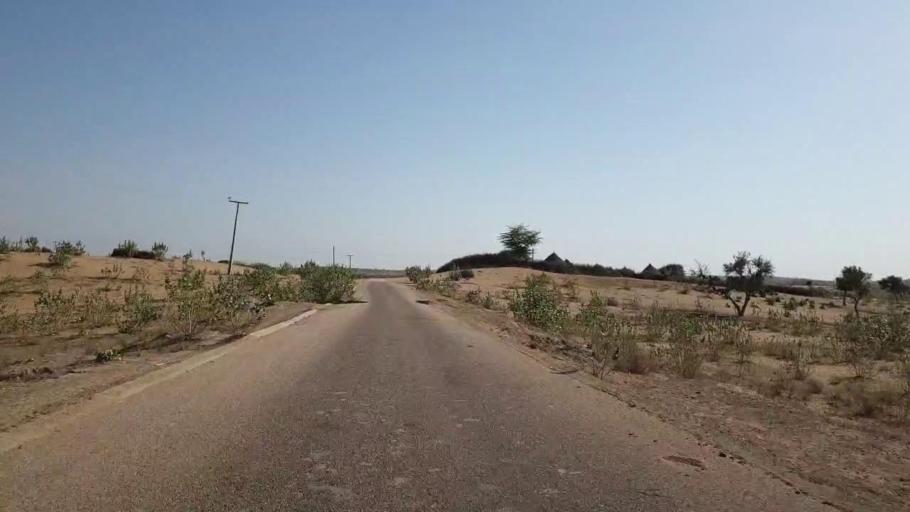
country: PK
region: Sindh
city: Nabisar
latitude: 25.1008
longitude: 70.0384
